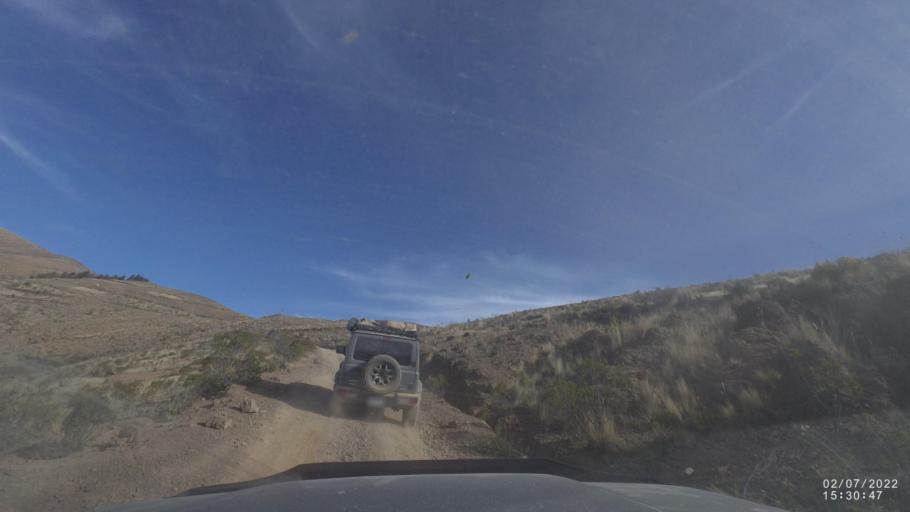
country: BO
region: Cochabamba
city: Irpa Irpa
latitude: -17.8818
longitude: -66.4138
